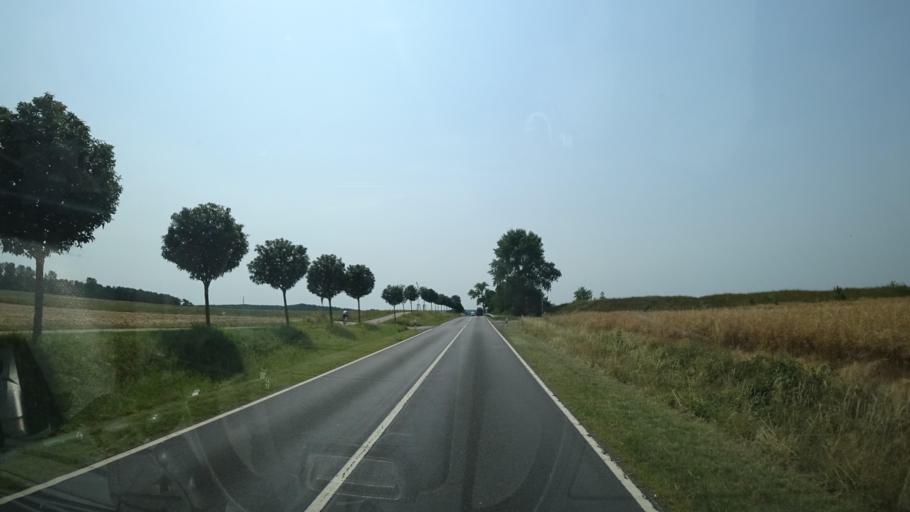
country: DE
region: Mecklenburg-Vorpommern
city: Loddin
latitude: 53.9498
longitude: 14.0509
